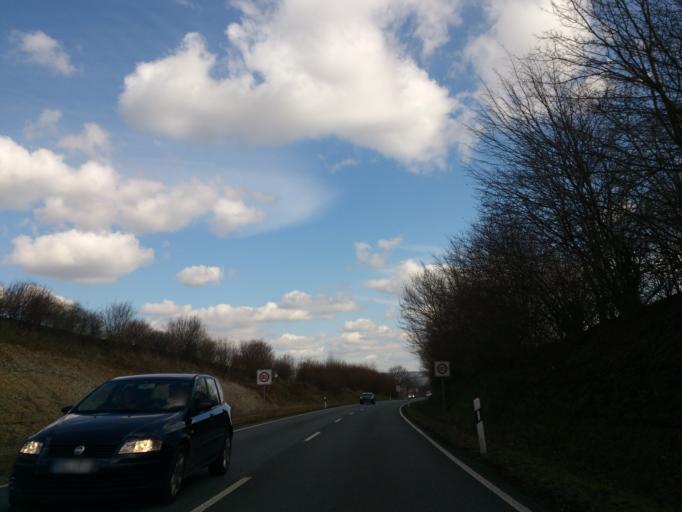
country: DE
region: North Rhine-Westphalia
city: Brakel
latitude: 51.7147
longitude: 9.2471
